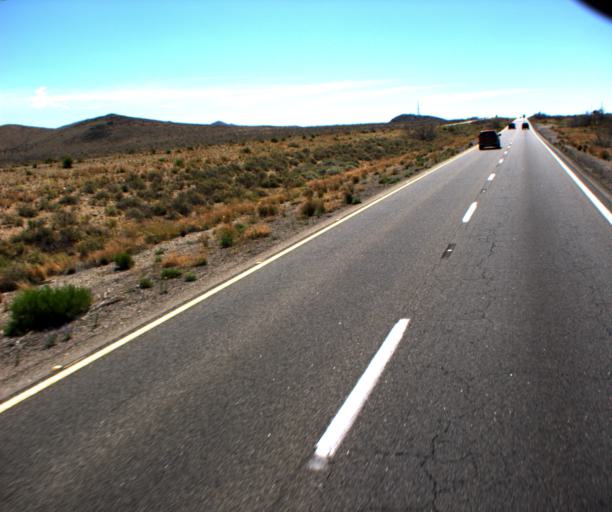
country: US
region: Arizona
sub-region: Mohave County
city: Dolan Springs
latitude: 35.4520
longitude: -114.2990
